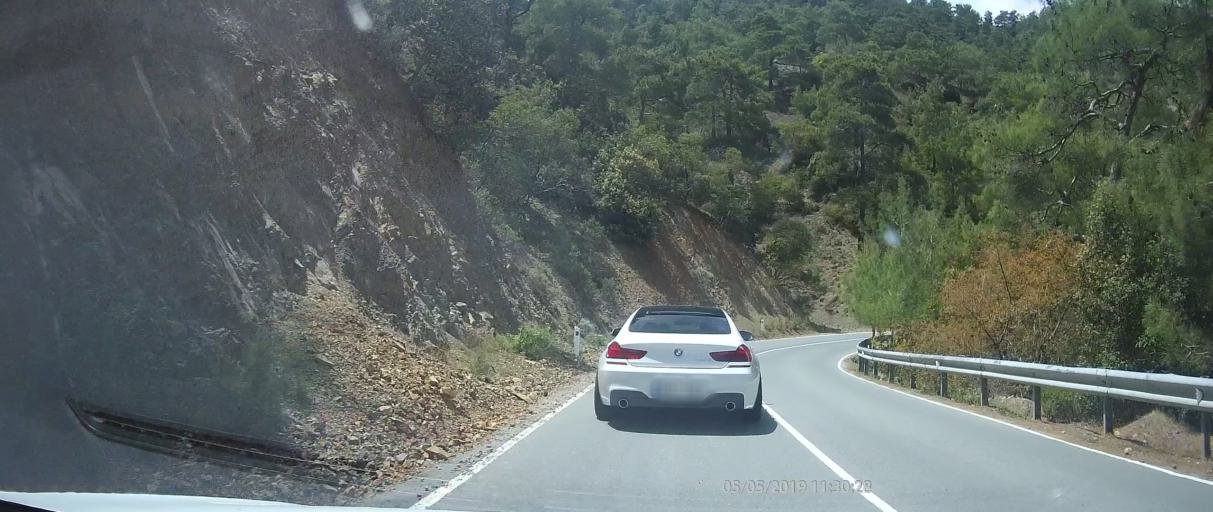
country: CY
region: Limassol
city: Pachna
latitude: 34.9454
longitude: 32.6475
